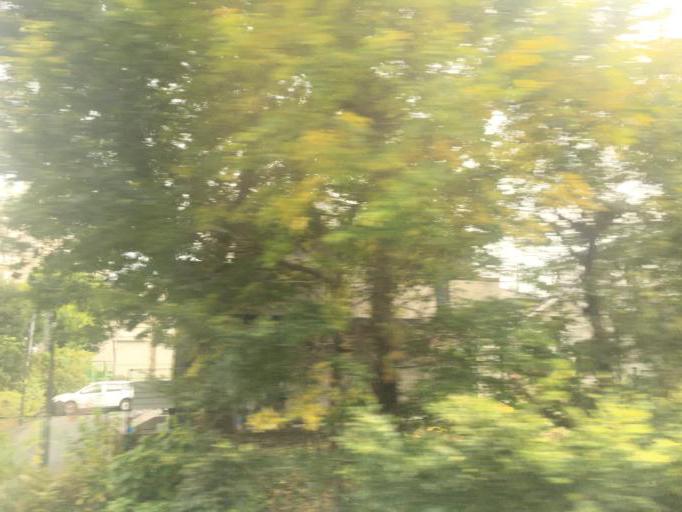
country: JP
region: Tokyo
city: Fussa
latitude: 35.7269
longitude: 139.3404
